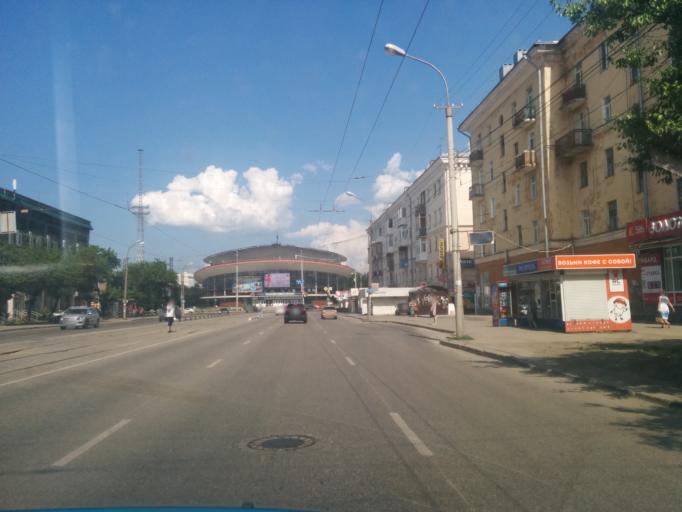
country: RU
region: Perm
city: Perm
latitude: 58.0185
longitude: 56.2782
